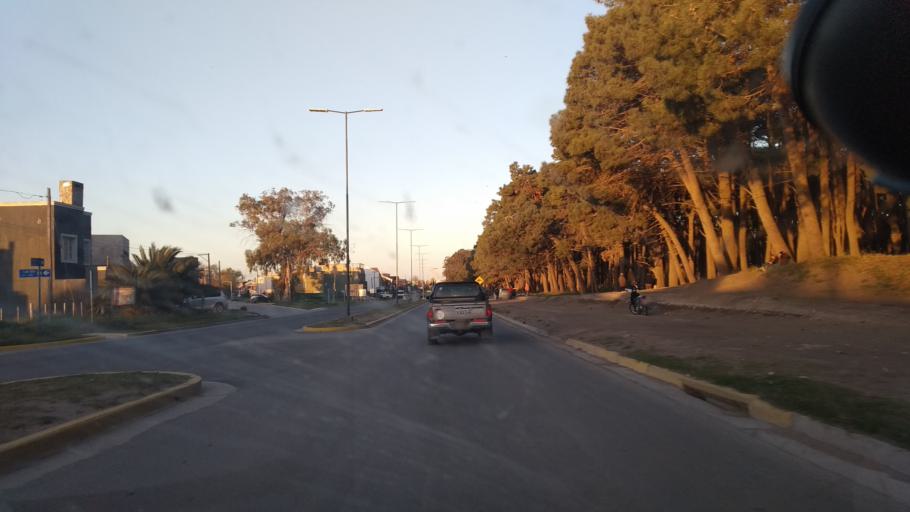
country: AR
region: Buenos Aires
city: Necochea
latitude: -38.5834
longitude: -58.7449
